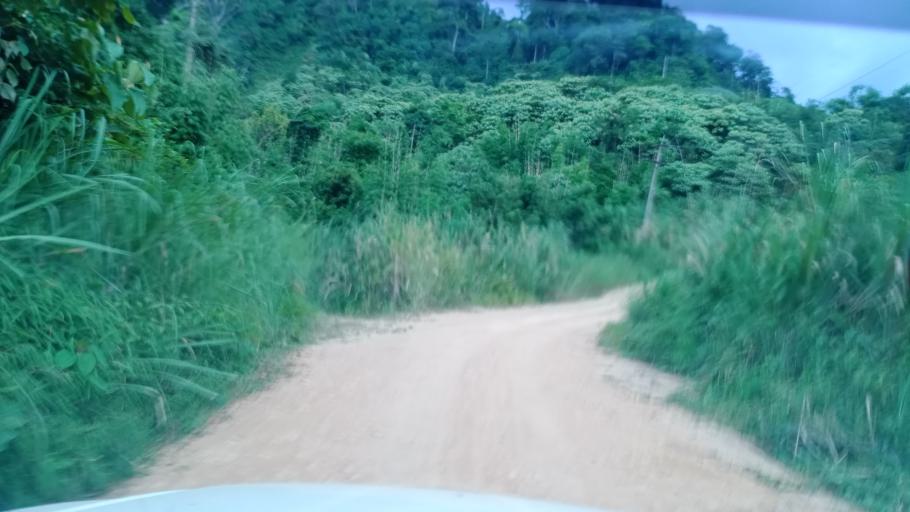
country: TH
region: Changwat Bueng Kan
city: Pak Khat
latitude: 18.7282
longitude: 103.2743
